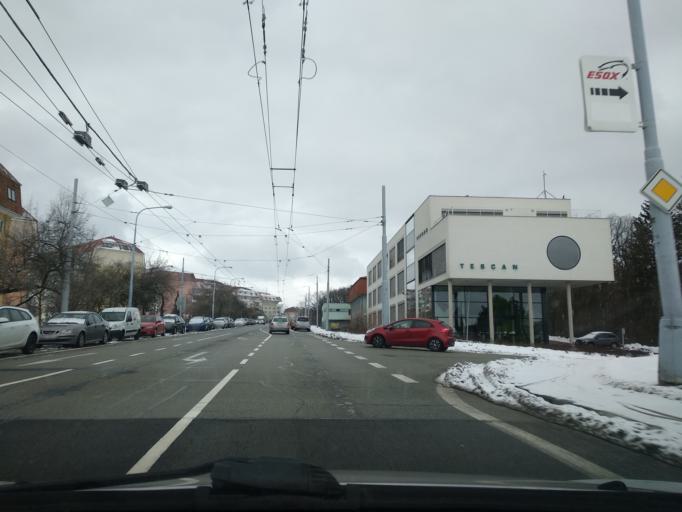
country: CZ
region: South Moravian
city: Troubsko
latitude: 49.1884
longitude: 16.5334
